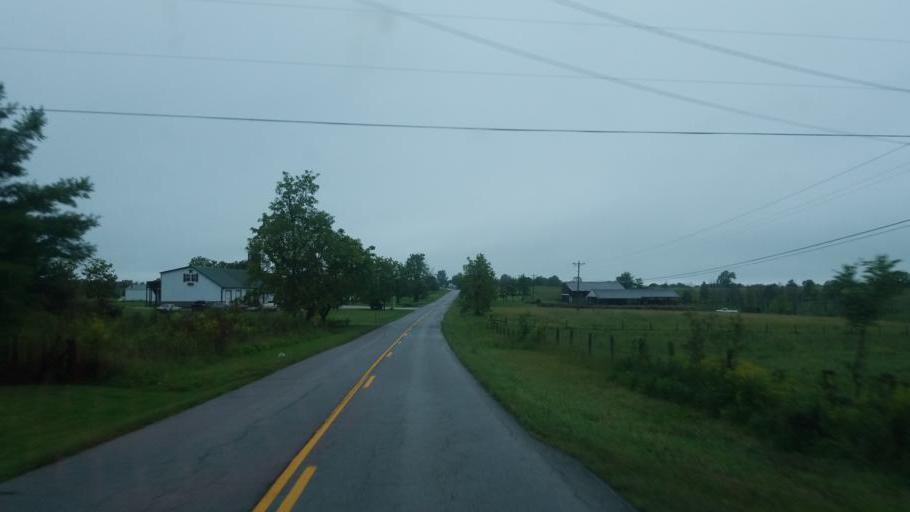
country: US
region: Kentucky
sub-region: Fleming County
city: Flemingsburg
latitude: 38.4094
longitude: -83.6515
